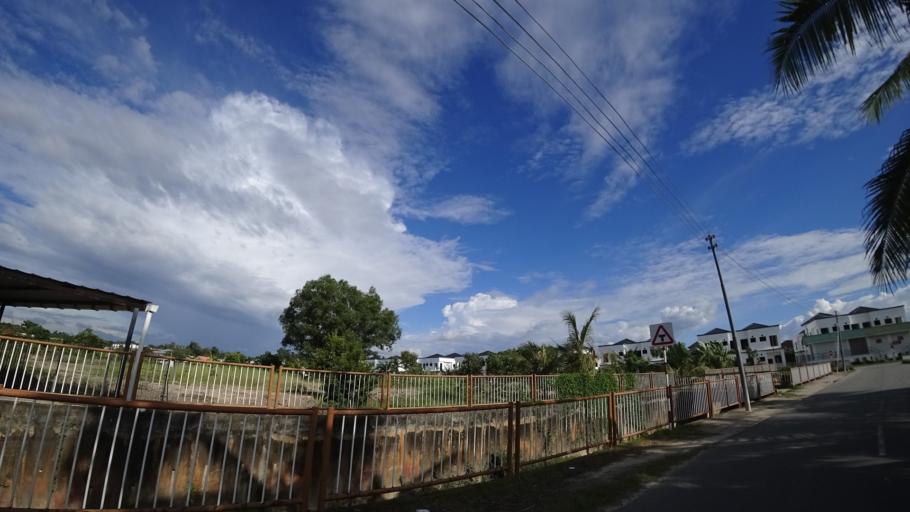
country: BN
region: Brunei and Muara
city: Bandar Seri Begawan
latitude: 4.8847
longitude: 114.8534
